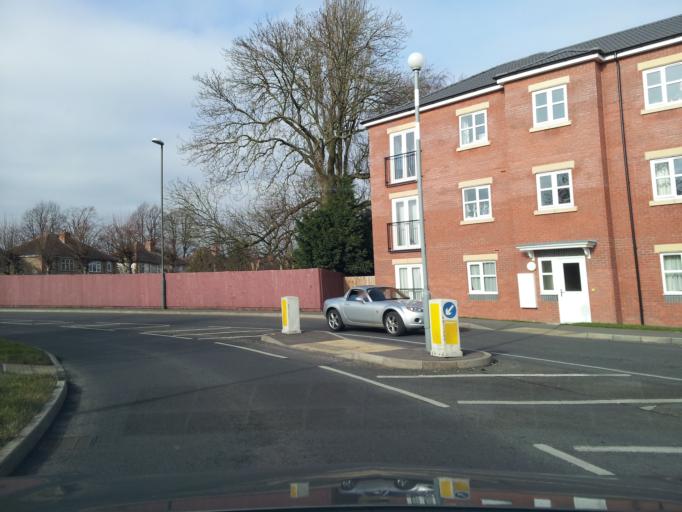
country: GB
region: England
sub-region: Derbyshire
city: Findern
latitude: 52.9101
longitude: -1.5286
